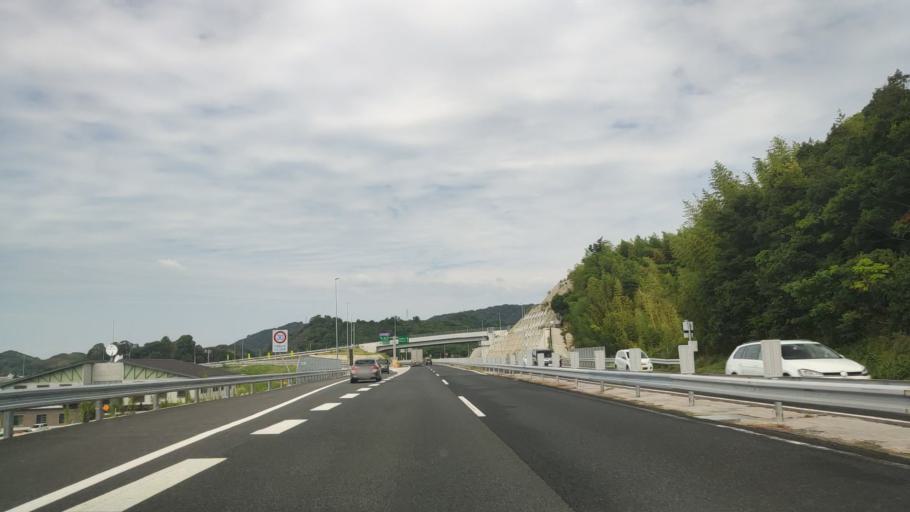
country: JP
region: Wakayama
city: Kainan
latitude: 34.2063
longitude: 135.2293
